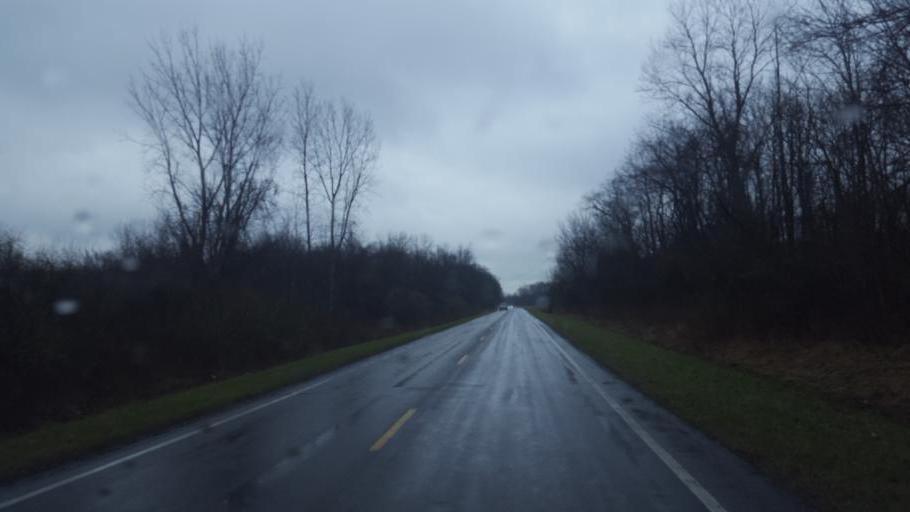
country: US
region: Ohio
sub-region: Delaware County
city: Lewis Center
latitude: 40.1857
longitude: -82.9519
